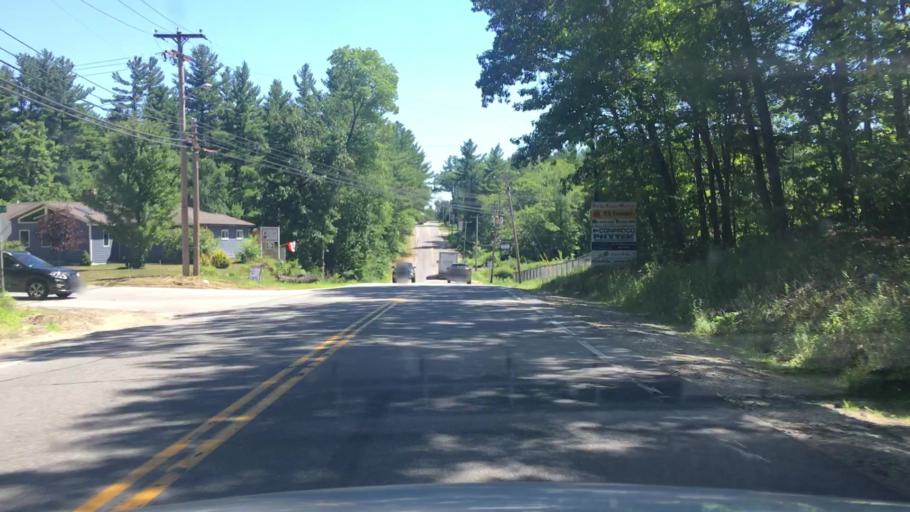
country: US
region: New Hampshire
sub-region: Merrimack County
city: Suncook
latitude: 43.1261
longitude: -71.4813
